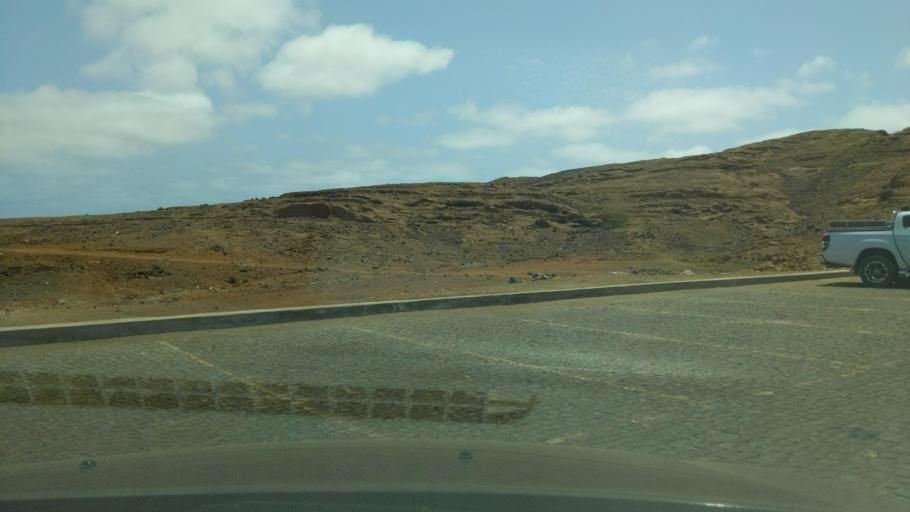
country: CV
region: Sal
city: Espargos
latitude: 16.7679
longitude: -22.8961
